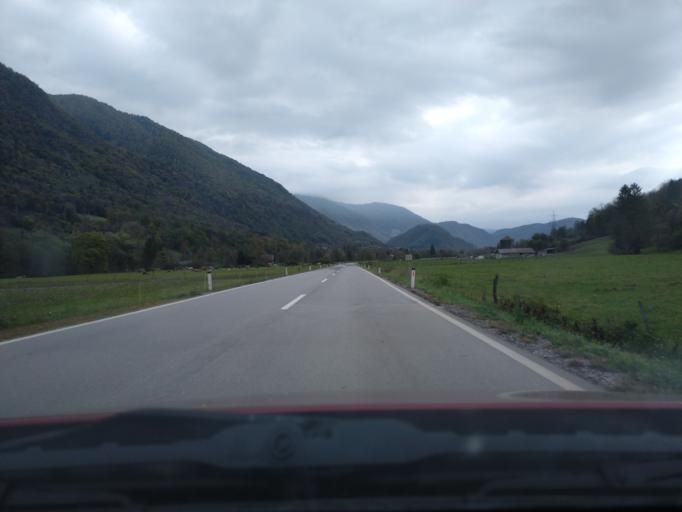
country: SI
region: Tolmin
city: Tolmin
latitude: 46.2039
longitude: 13.6777
